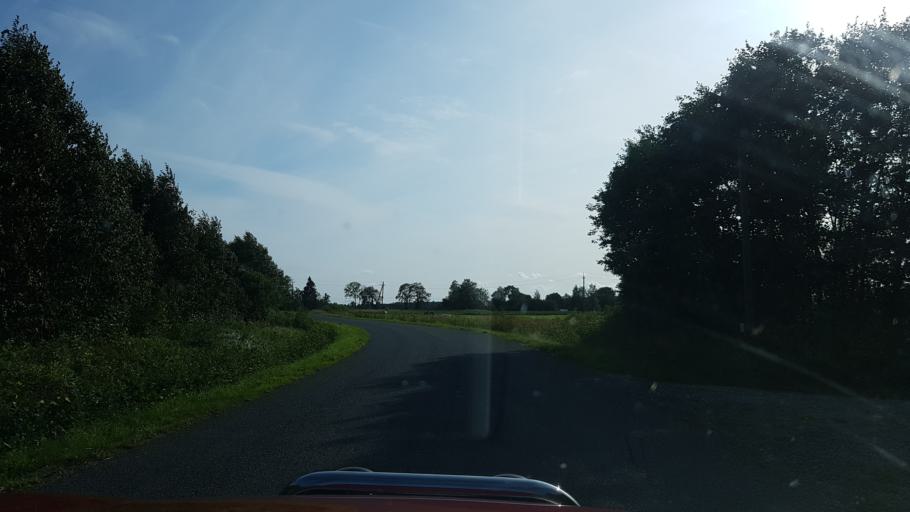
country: EE
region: Laeaene
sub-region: Lihula vald
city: Lihula
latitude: 58.3838
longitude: 24.0082
